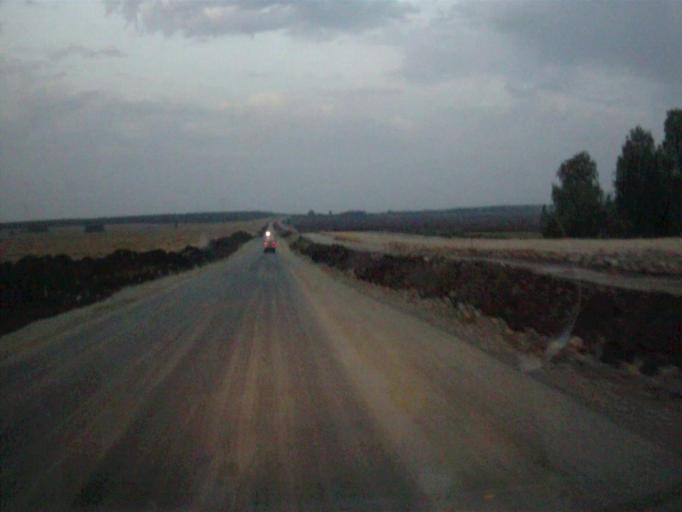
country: RU
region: Chelyabinsk
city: Timiryazevskiy
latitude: 55.2068
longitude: 60.7990
